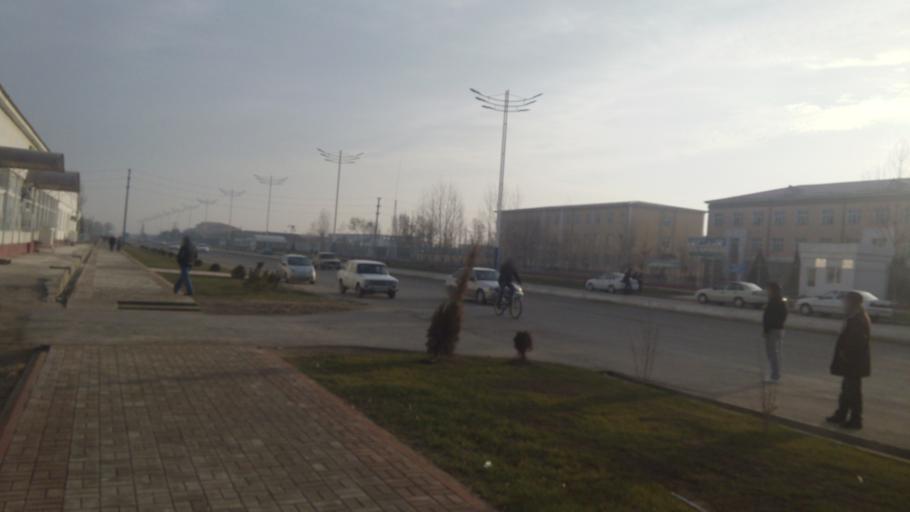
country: UZ
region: Sirdaryo
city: Guliston
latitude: 40.5137
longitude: 68.7830
